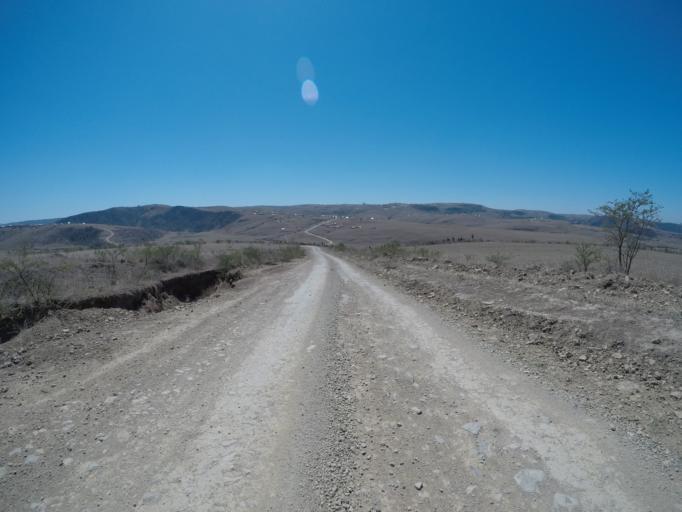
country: ZA
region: Eastern Cape
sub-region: OR Tambo District Municipality
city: Mthatha
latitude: -31.8745
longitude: 28.8724
